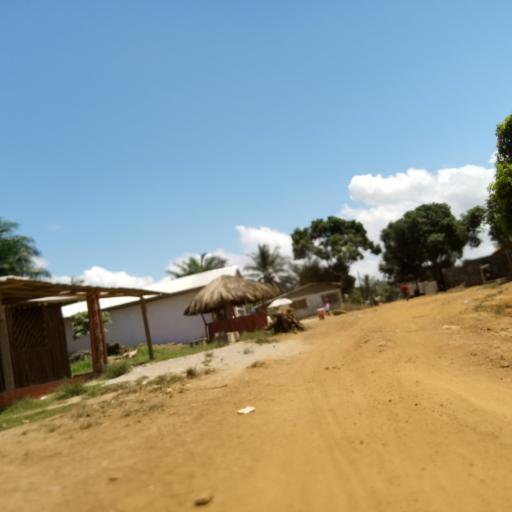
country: LR
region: Montserrado
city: Monrovia
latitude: 6.2493
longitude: -10.6903
